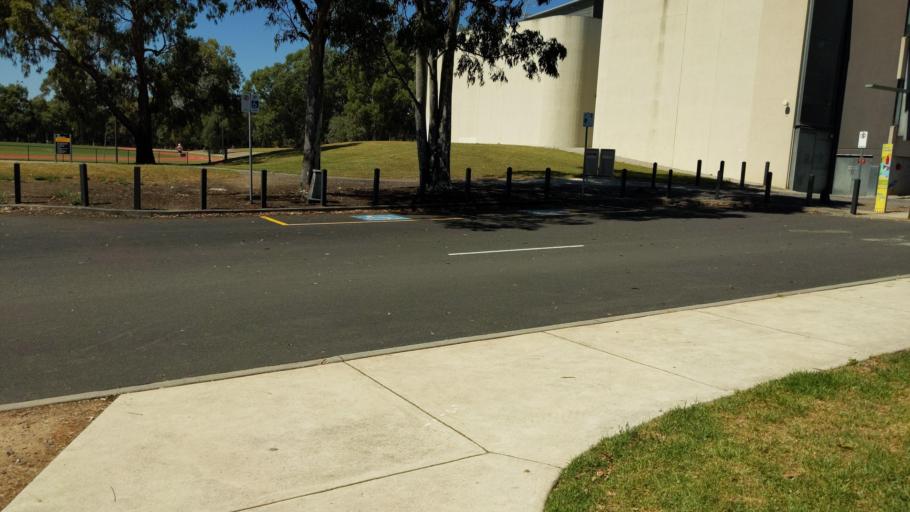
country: AU
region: Victoria
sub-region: Whittlesea
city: Mill Park
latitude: -37.6790
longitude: 145.0627
